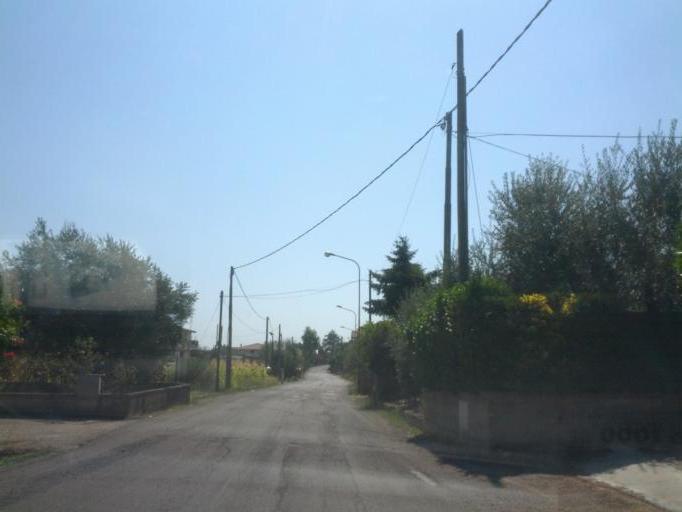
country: IT
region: Latium
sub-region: Provincia di Latina
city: Monte San Biagio
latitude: 41.3627
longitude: 13.3534
